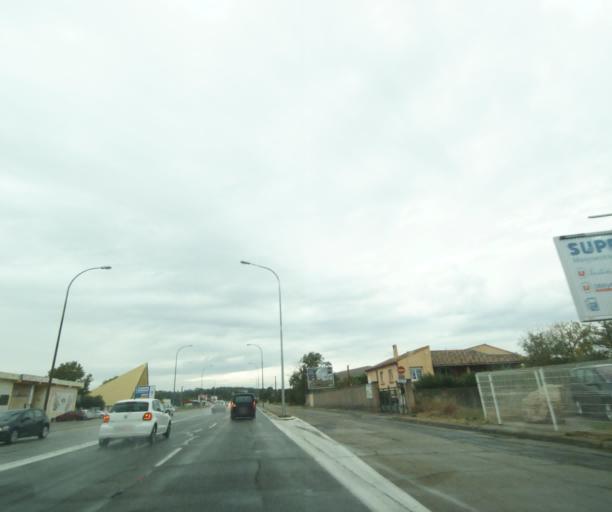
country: FR
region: Languedoc-Roussillon
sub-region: Departement du Gard
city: Rodilhan
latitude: 43.8543
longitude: 4.4019
